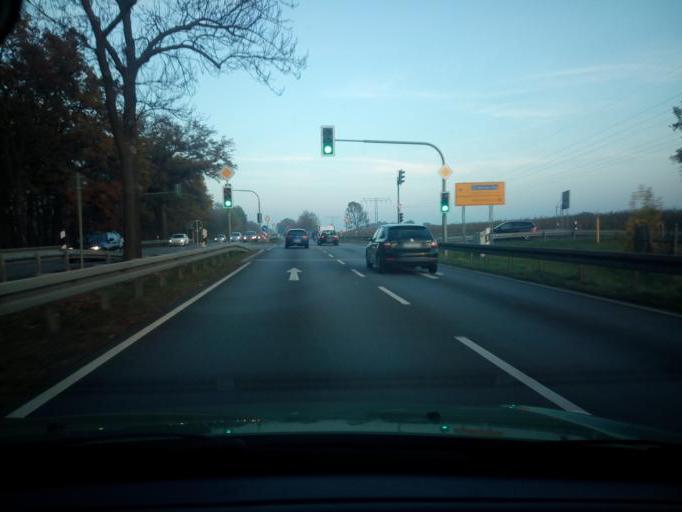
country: DE
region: Brandenburg
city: Hoppegarten
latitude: 52.5007
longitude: 13.6792
